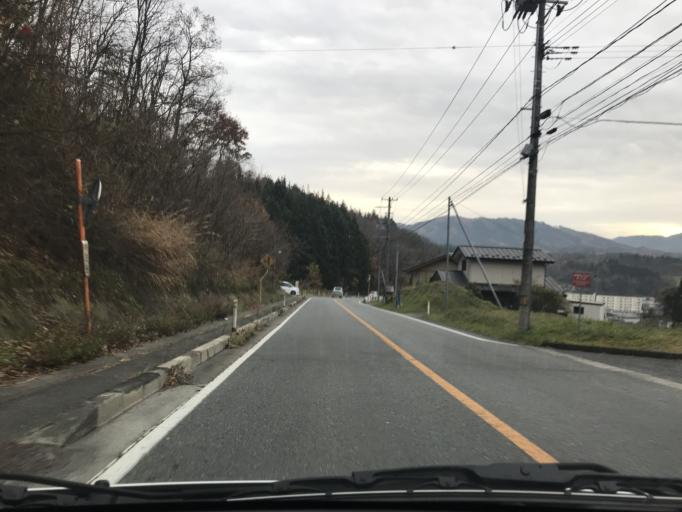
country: JP
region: Iwate
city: Ichinoseki
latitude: 39.0001
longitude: 141.3236
